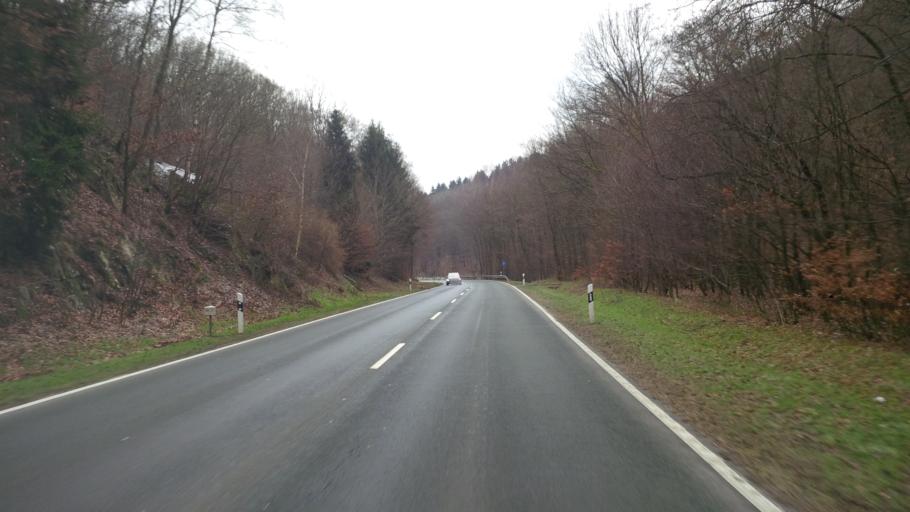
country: DE
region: Hesse
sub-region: Regierungsbezirk Darmstadt
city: Kronberg
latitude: 50.2240
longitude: 8.5191
